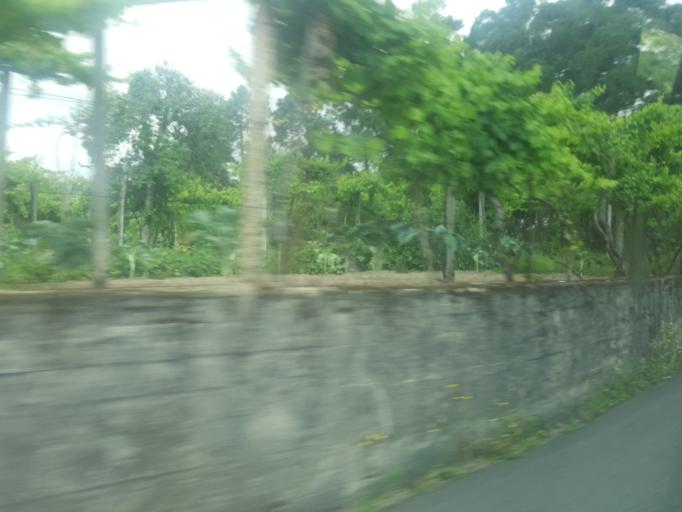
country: PT
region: Porto
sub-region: Marco de Canaveses
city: Marco de Canavezes
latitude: 41.1875
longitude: -8.1899
